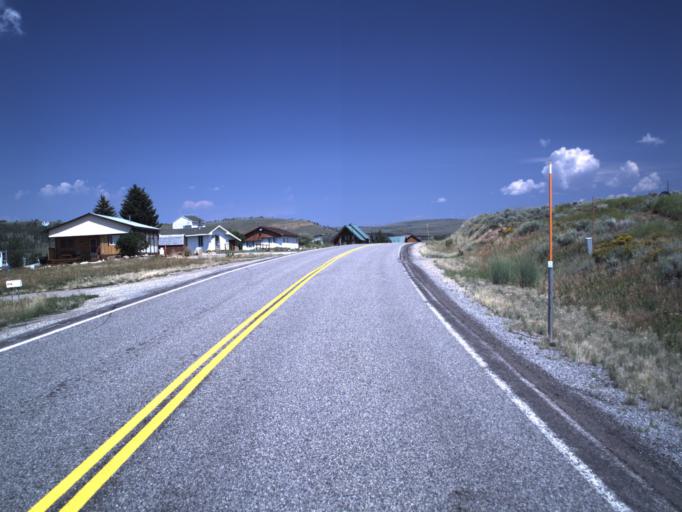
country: US
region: Utah
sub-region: Carbon County
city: Helper
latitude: 39.8012
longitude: -111.1343
